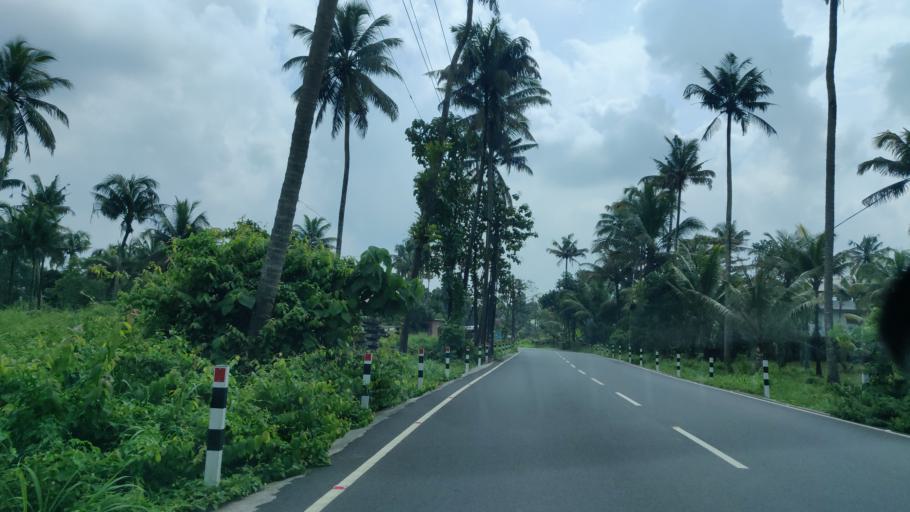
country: IN
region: Kerala
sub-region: Ernakulam
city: Angamali
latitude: 10.1673
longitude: 76.4168
